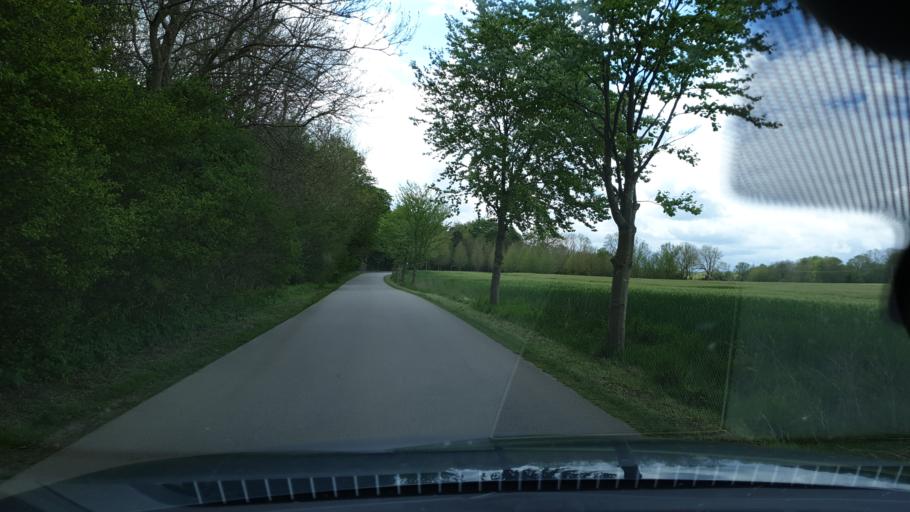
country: DE
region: Mecklenburg-Vorpommern
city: Jurgenshagen
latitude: 53.9347
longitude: 11.8751
